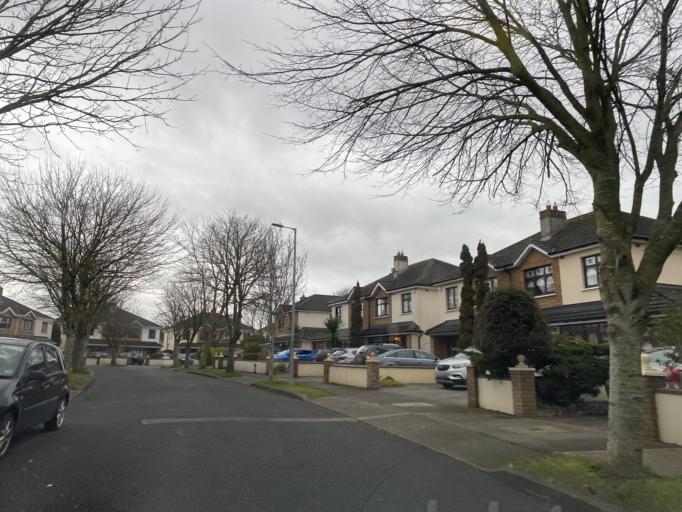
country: IE
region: Leinster
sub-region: Kildare
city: Celbridge
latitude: 53.3521
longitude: -6.5519
